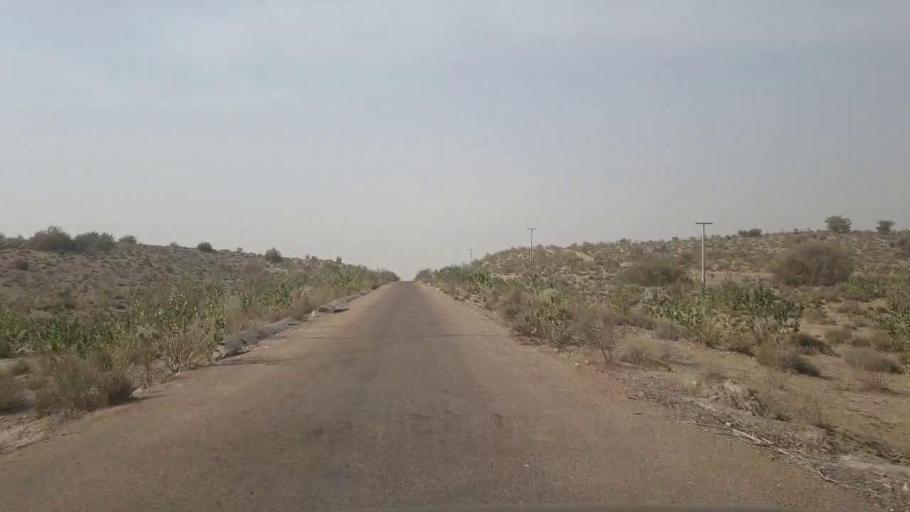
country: PK
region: Sindh
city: Chor
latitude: 25.6112
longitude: 69.9331
